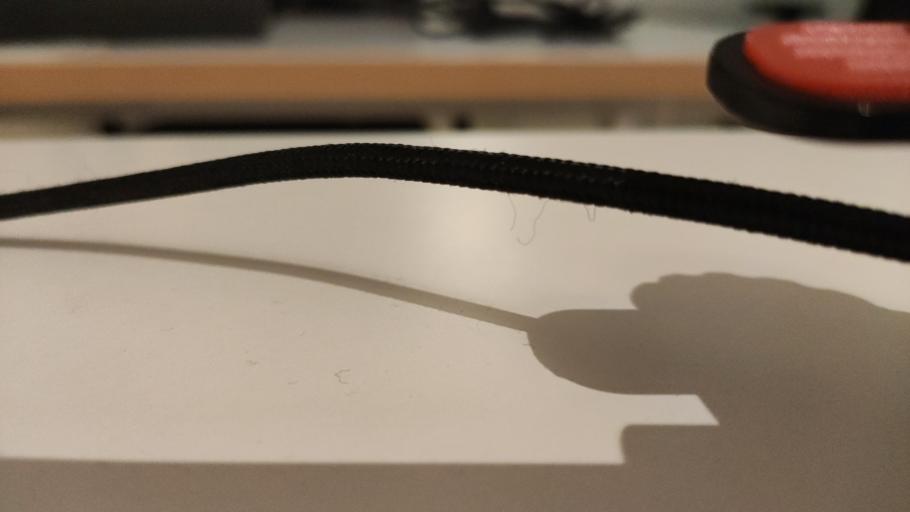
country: RU
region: Moskovskaya
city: Kurovskoye
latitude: 55.5420
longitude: 38.8731
